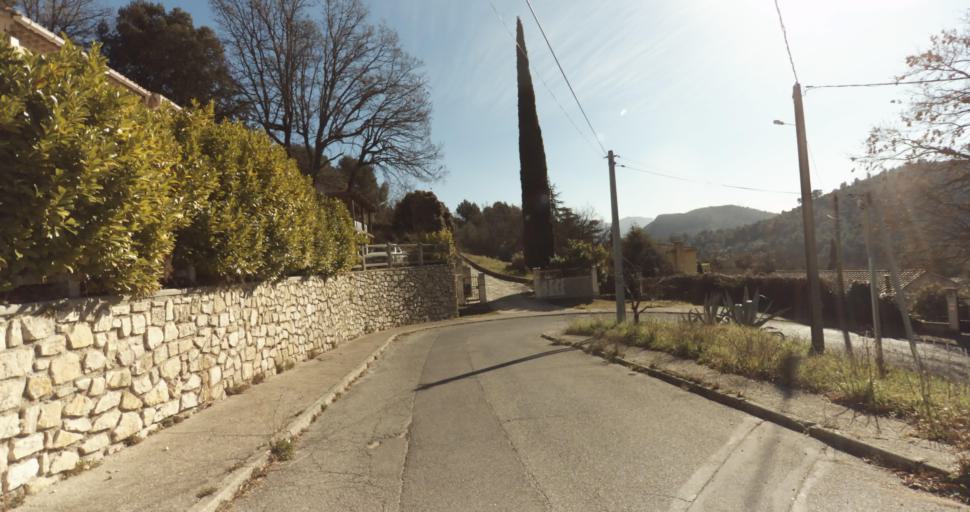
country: FR
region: Provence-Alpes-Cote d'Azur
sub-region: Departement des Bouches-du-Rhone
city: Peypin
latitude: 43.3819
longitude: 5.5848
